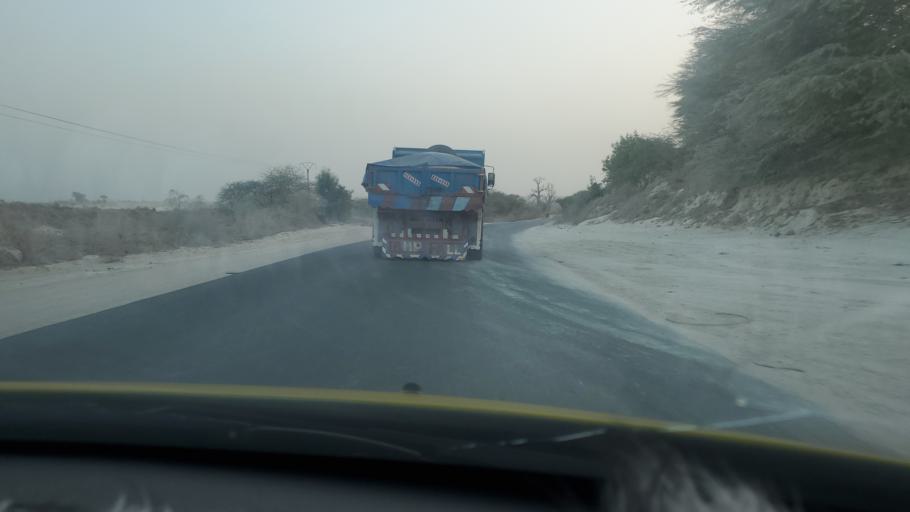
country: SN
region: Thies
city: Nguekhokh
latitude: 14.6356
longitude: -16.9928
